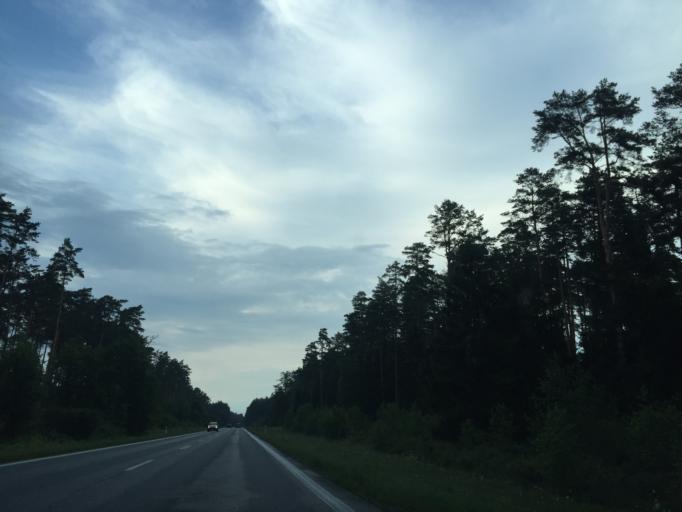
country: PL
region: Masovian Voivodeship
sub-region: Powiat ostrowski
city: Brok
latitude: 52.7362
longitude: 21.8522
